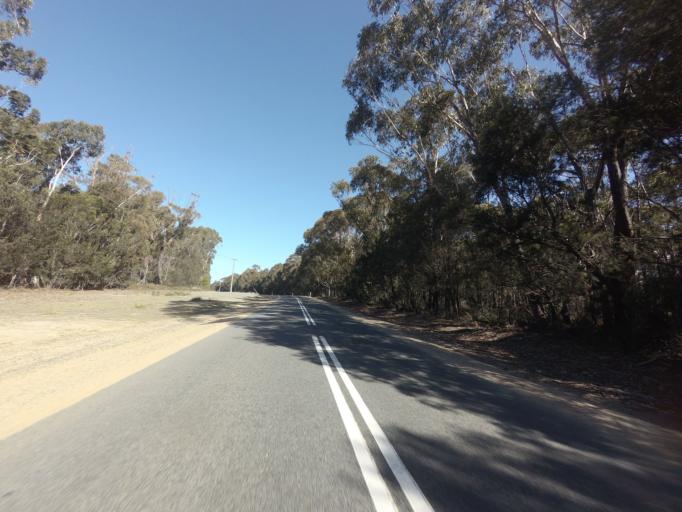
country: AU
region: Tasmania
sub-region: Break O'Day
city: St Helens
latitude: -41.6797
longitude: 148.2790
